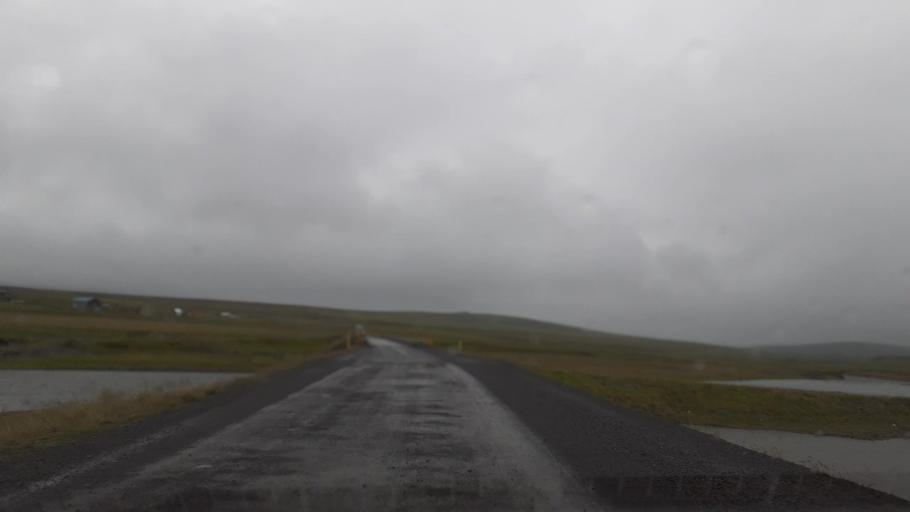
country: IS
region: East
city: Egilsstadir
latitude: 66.0413
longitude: -15.1000
